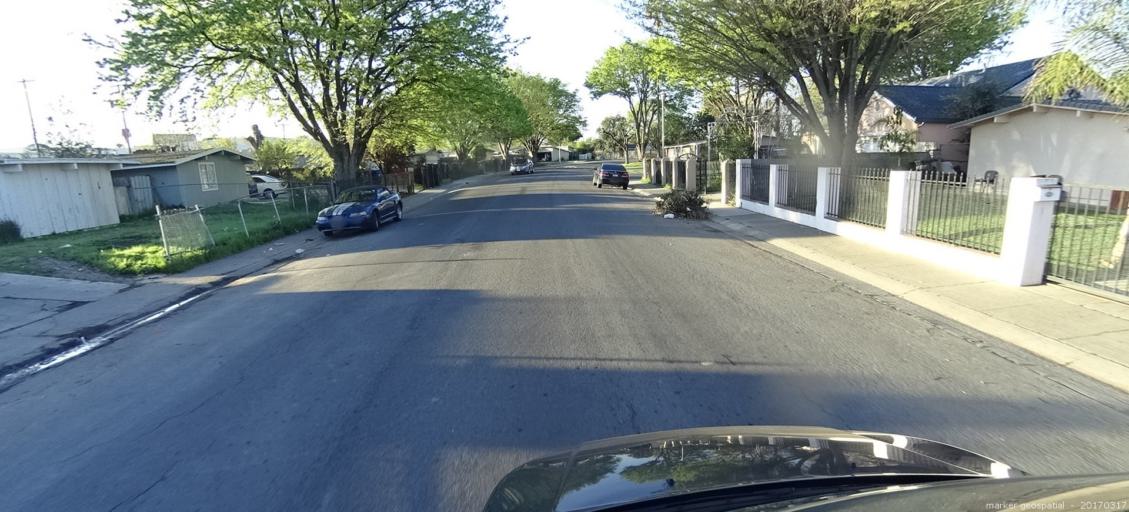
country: US
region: California
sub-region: Sacramento County
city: Parkway
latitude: 38.4954
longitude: -121.4858
